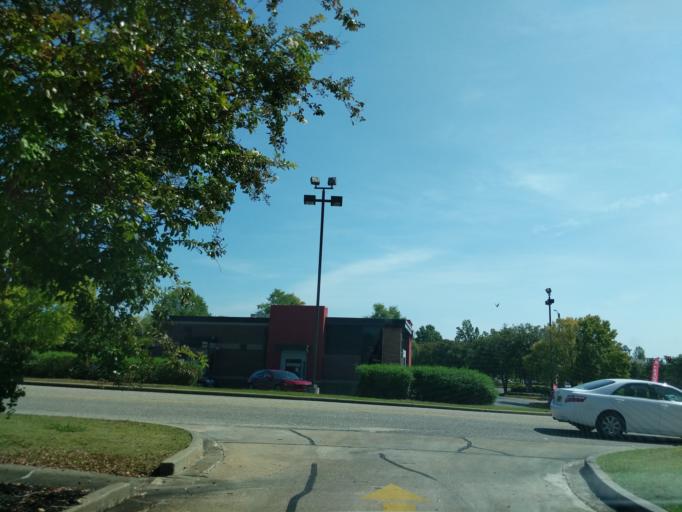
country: US
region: Alabama
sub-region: Montgomery County
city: Pike Road
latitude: 32.3585
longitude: -86.1701
